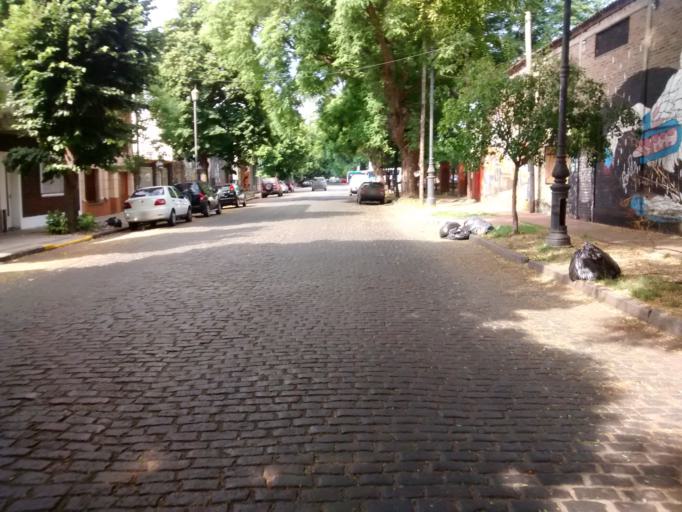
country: AR
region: Buenos Aires
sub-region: Partido de La Plata
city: La Plata
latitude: -34.9404
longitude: -57.9402
